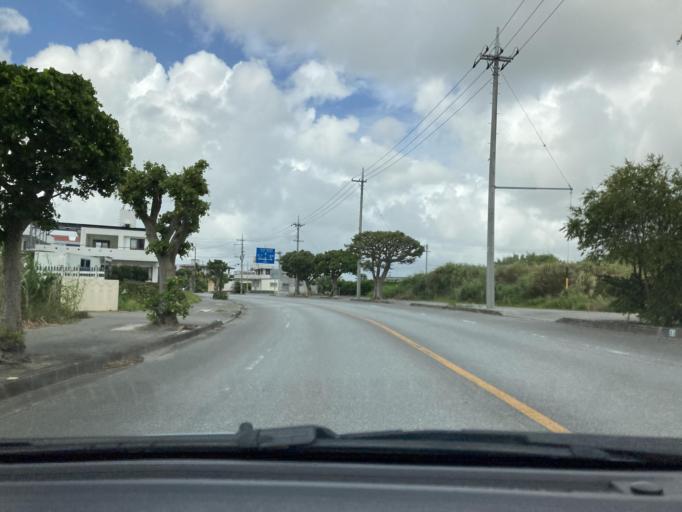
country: JP
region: Okinawa
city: Itoman
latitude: 26.1433
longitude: 127.6934
